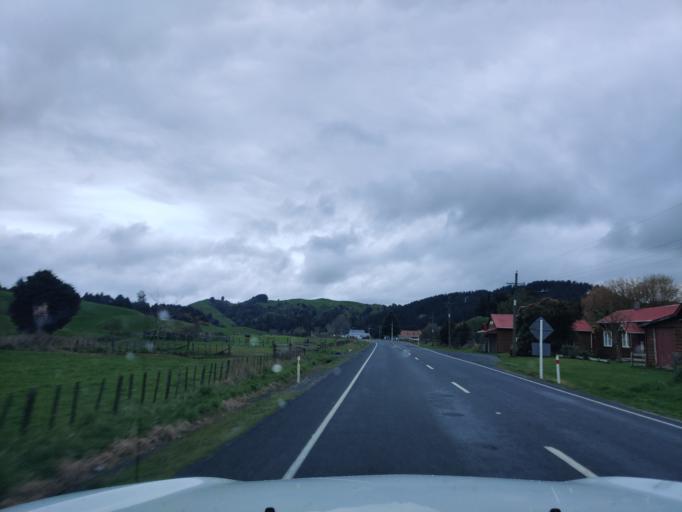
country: NZ
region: Waikato
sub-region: Otorohanga District
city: Otorohanga
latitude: -38.5817
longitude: 175.2159
